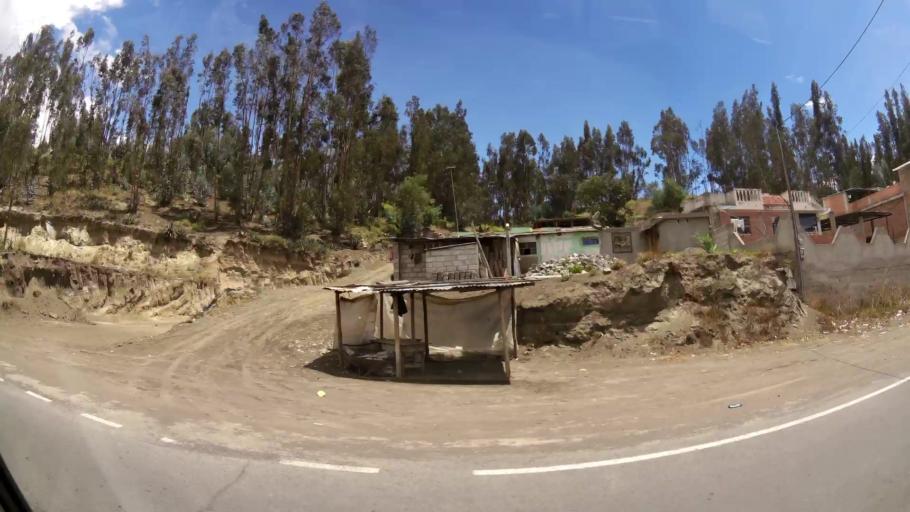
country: EC
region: Tungurahua
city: Ambato
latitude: -1.2797
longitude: -78.5906
